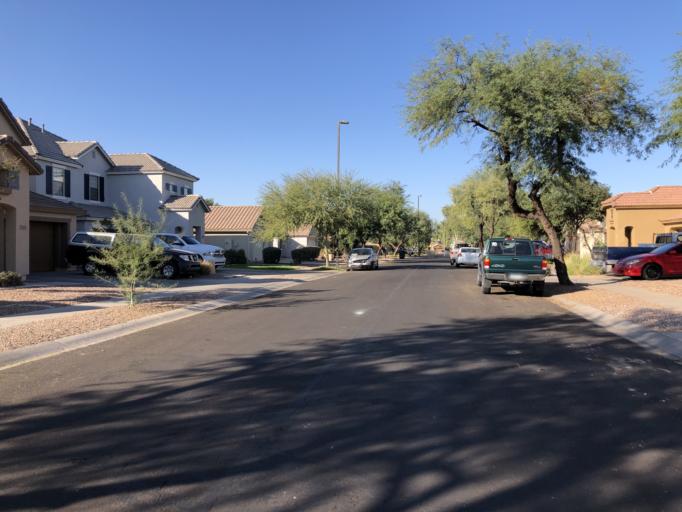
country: US
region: Arizona
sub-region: Maricopa County
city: Queen Creek
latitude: 33.2709
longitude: -111.7059
